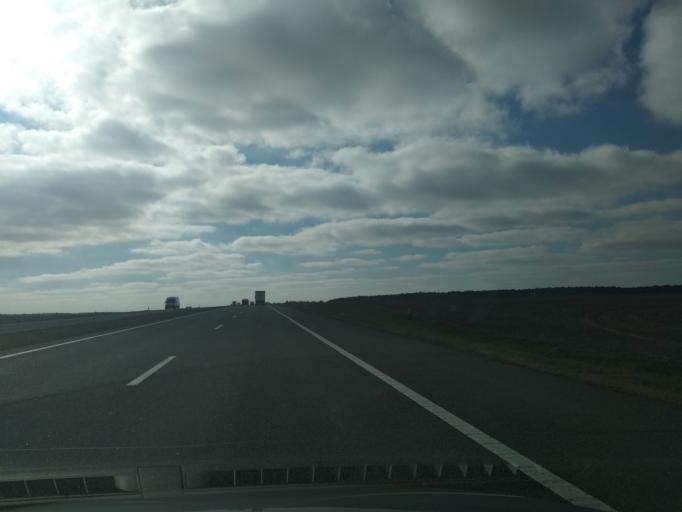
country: BY
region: Grodnenskaya
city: Mir
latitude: 53.4270
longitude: 26.5813
